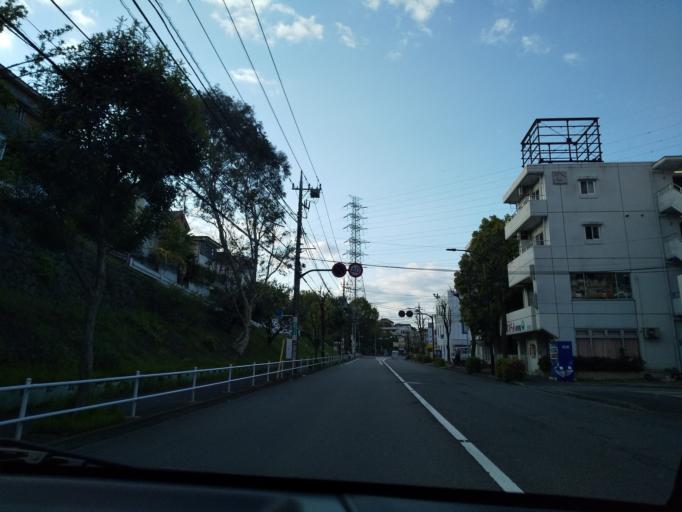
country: JP
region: Tokyo
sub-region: Machida-shi
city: Machida
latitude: 35.5561
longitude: 139.4267
